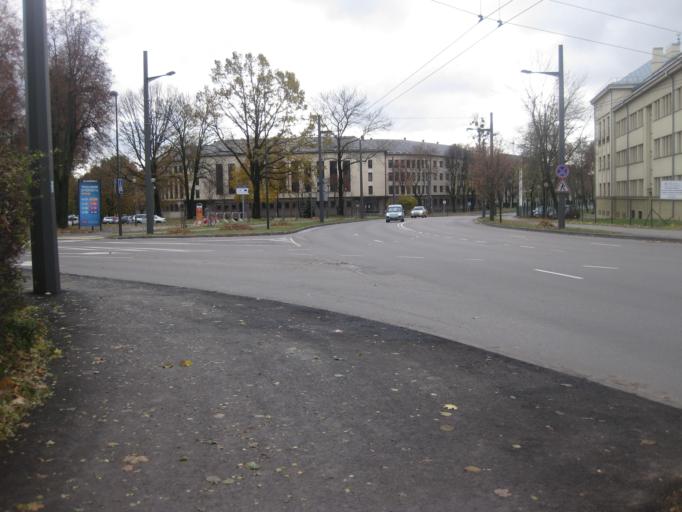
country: LT
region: Kauno apskritis
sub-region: Kaunas
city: Eiguliai
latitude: 54.9067
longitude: 23.9313
